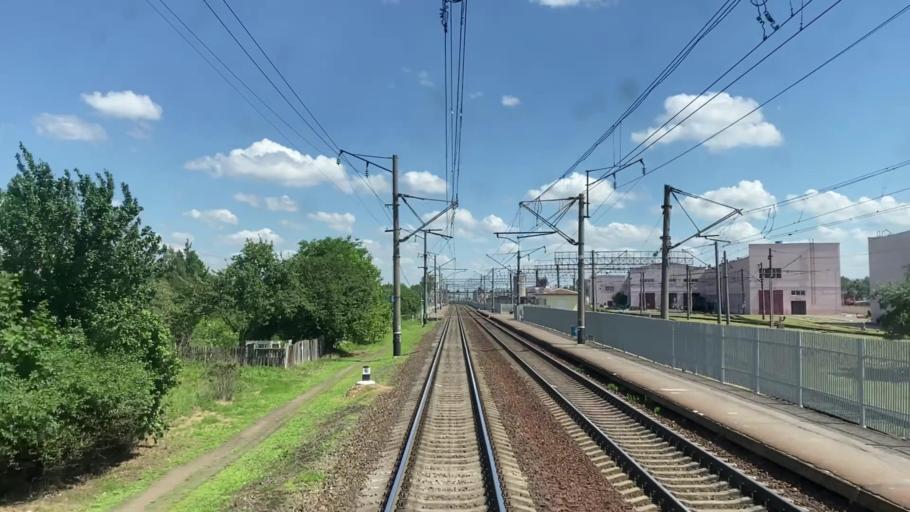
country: BY
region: Brest
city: Baranovichi
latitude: 53.1184
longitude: 25.9697
